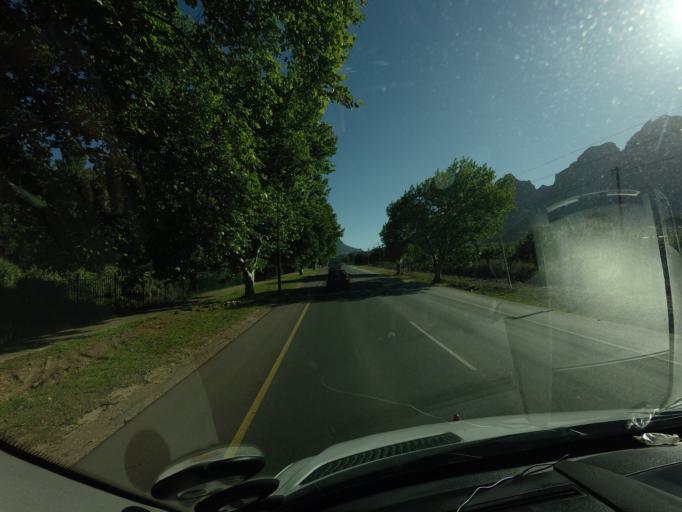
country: ZA
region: Western Cape
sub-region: Cape Winelands District Municipality
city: Stellenbosch
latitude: -33.8829
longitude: 18.9686
